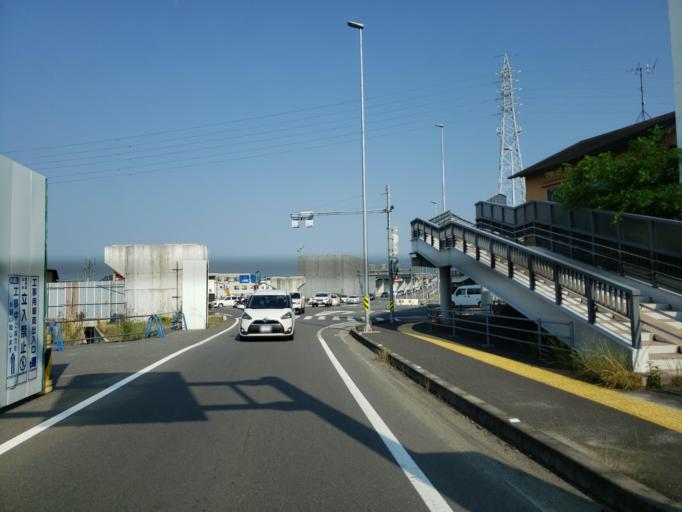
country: JP
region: Ehime
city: Masaki-cho
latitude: 33.8110
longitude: 132.7332
